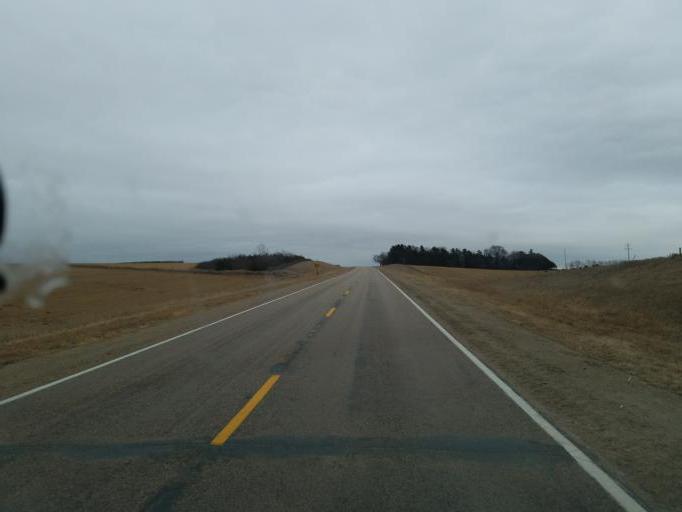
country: US
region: Nebraska
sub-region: Knox County
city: Bloomfield
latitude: 42.5978
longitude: -97.6003
